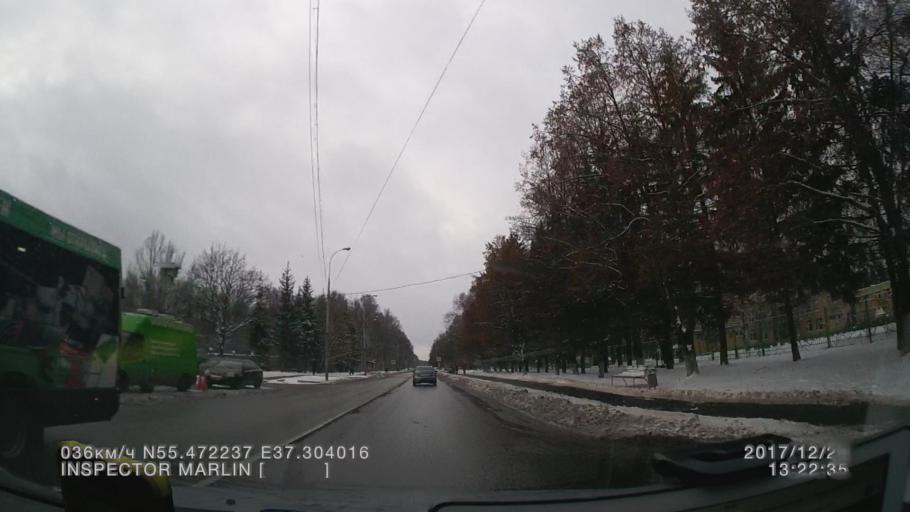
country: RU
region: Moskovskaya
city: Troitsk
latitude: 55.4722
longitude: 37.3039
